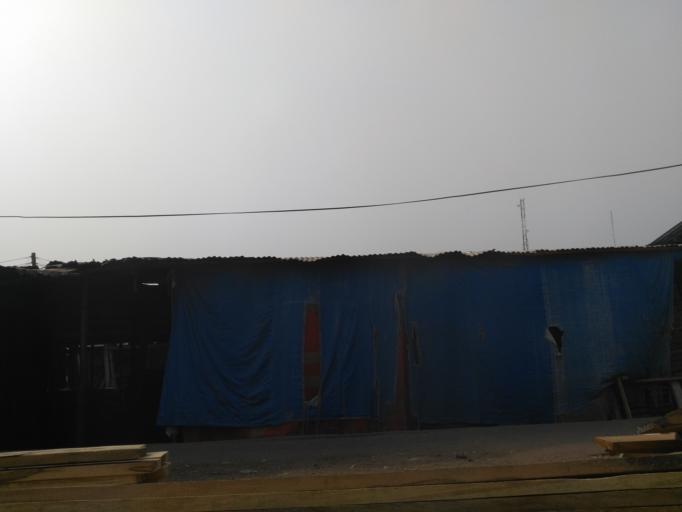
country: GH
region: Ashanti
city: Kumasi
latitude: 6.6973
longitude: -1.6119
